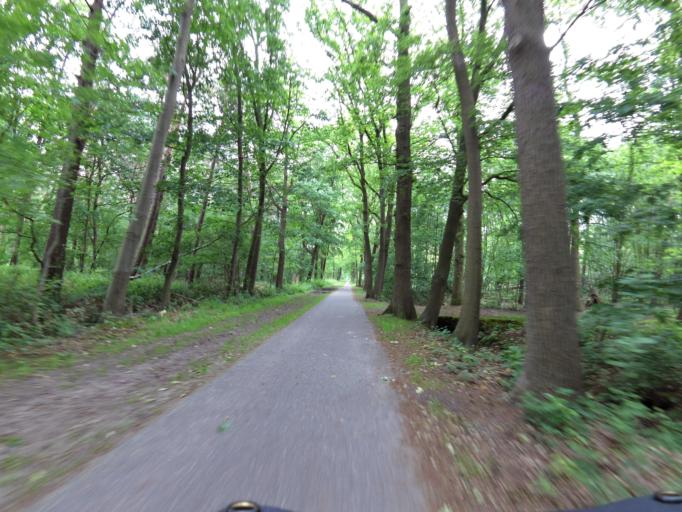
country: NL
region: North Brabant
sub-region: Gemeente Breda
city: Breda
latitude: 51.5495
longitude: 4.8075
